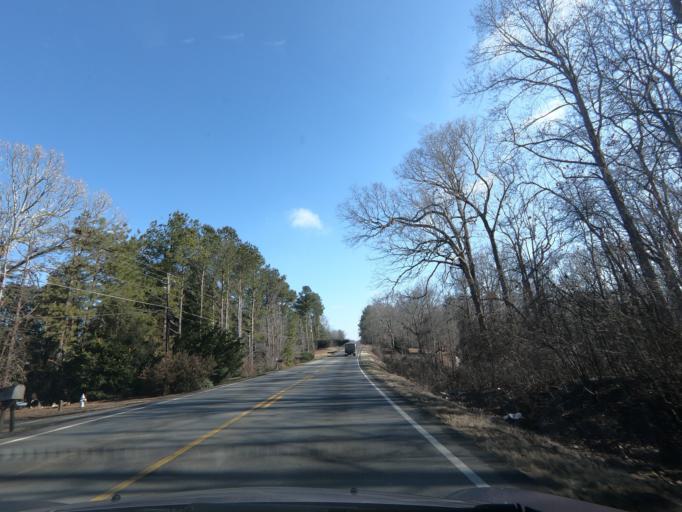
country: US
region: Georgia
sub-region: Cherokee County
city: Ball Ground
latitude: 34.2823
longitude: -84.2935
